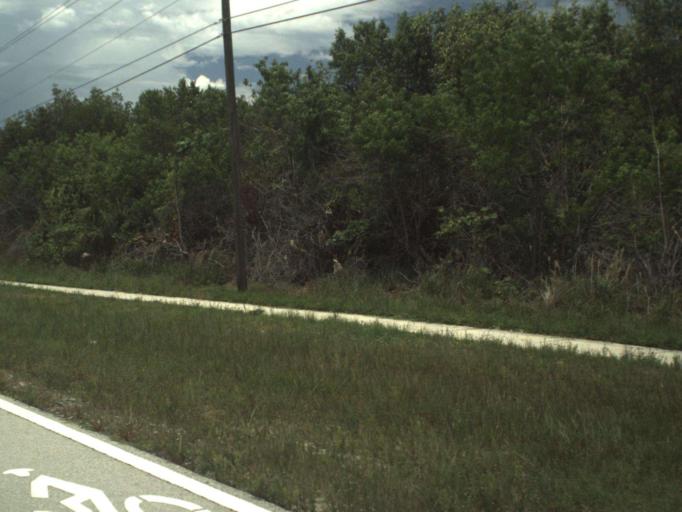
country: US
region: Florida
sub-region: Saint Lucie County
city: Hutchinson Island South
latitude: 27.3331
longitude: -80.2338
